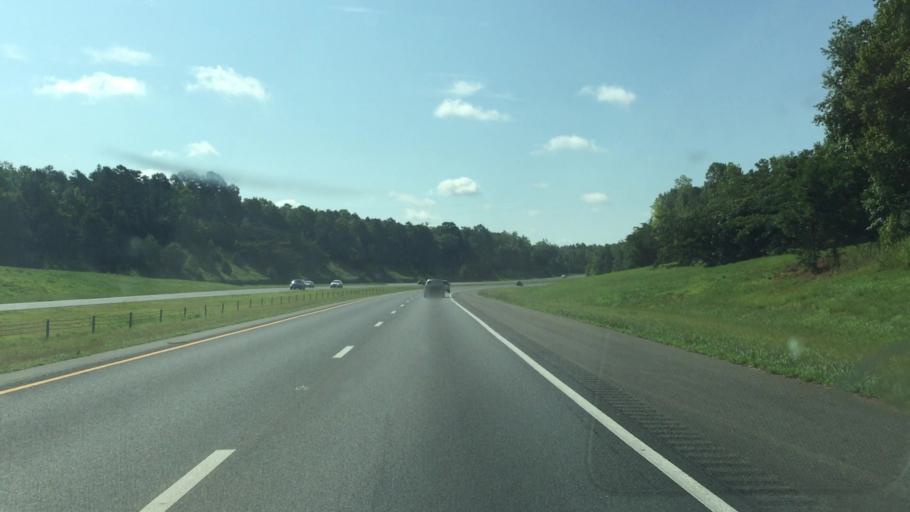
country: US
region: North Carolina
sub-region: Mecklenburg County
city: Mint Hill
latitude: 35.2014
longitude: -80.6327
